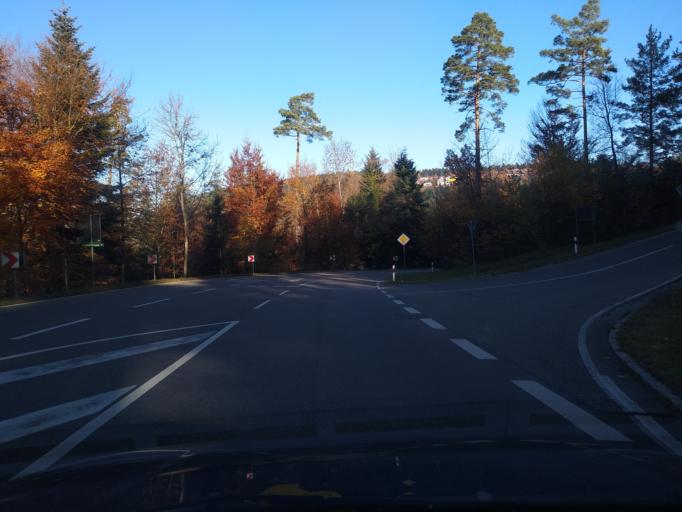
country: DE
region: Baden-Wuerttemberg
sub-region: Karlsruhe Region
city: Bad Liebenzell
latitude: 48.7765
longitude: 8.7394
